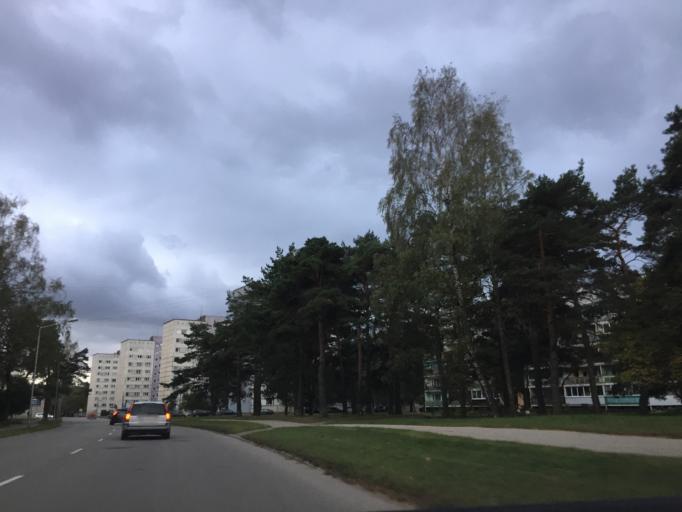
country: LV
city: Tireli
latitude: 56.9623
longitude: 23.6028
